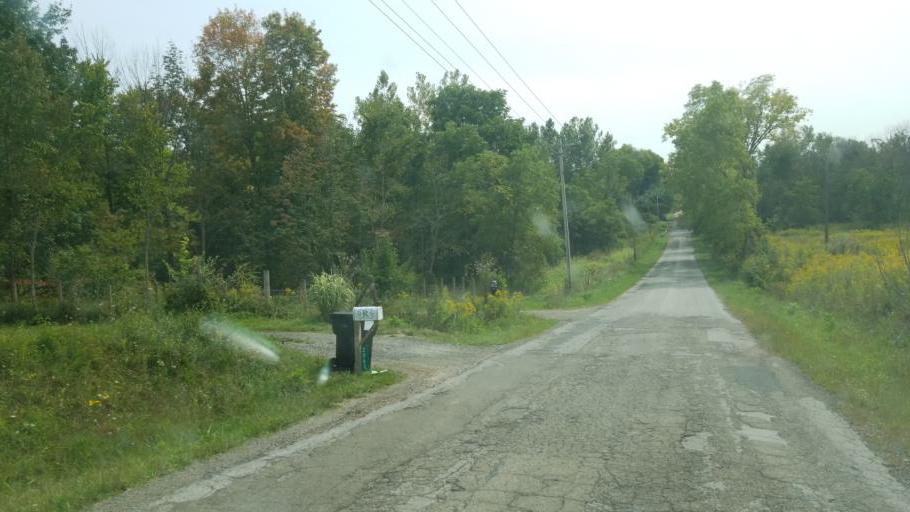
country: US
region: Ohio
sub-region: Knox County
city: Fredericktown
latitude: 40.4220
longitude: -82.6504
